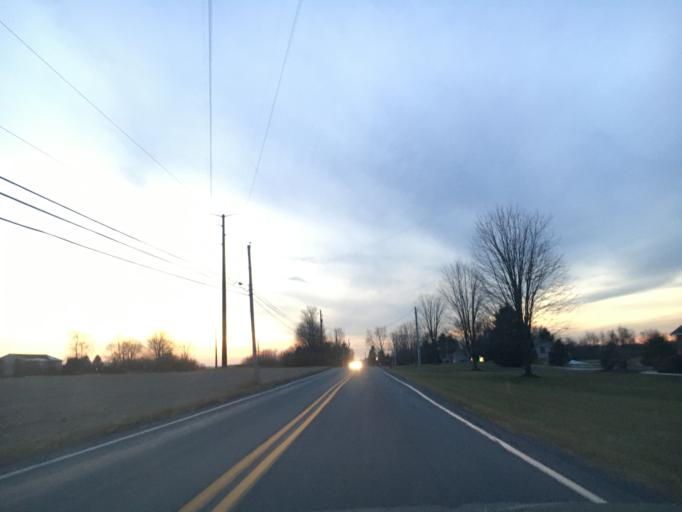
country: US
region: Pennsylvania
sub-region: Northampton County
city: Youngsville
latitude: 40.7624
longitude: -75.4529
